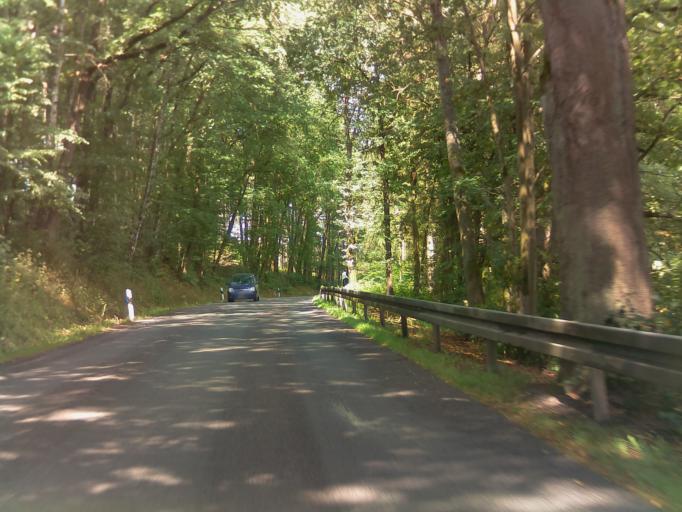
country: DE
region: Hesse
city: Grebenau
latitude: 50.7250
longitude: 9.4598
